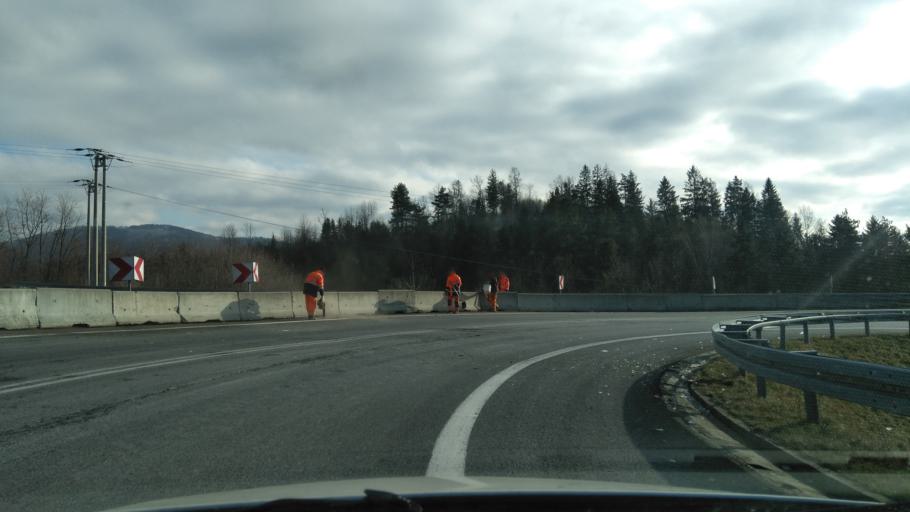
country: PL
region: Silesian Voivodeship
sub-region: Powiat zywiecki
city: Milowka
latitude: 49.5680
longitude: 19.0780
